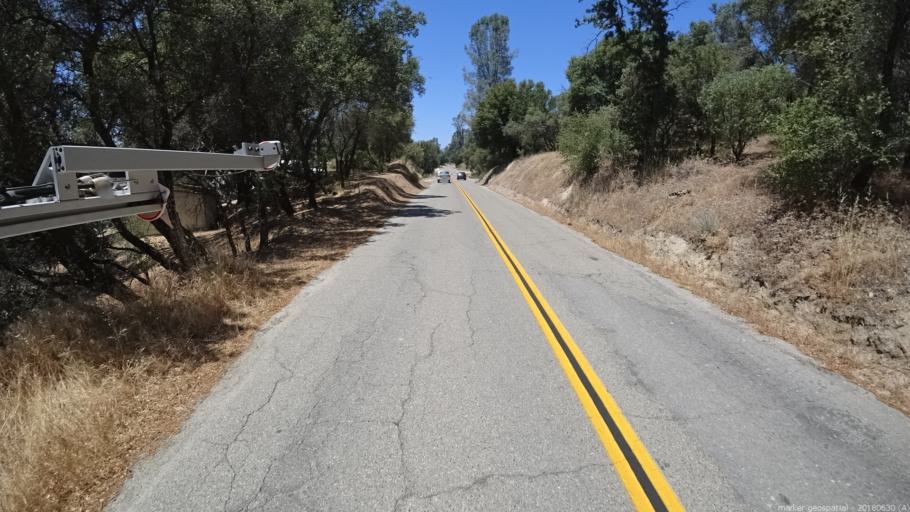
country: US
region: California
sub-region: Fresno County
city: Auberry
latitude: 37.2168
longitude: -119.4834
